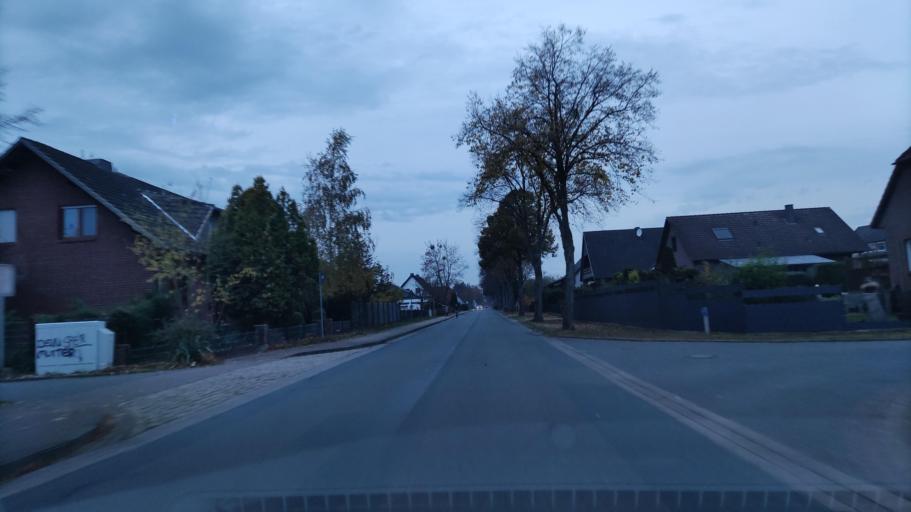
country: DE
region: Lower Saxony
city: Parsau
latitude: 52.5370
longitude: 10.8887
